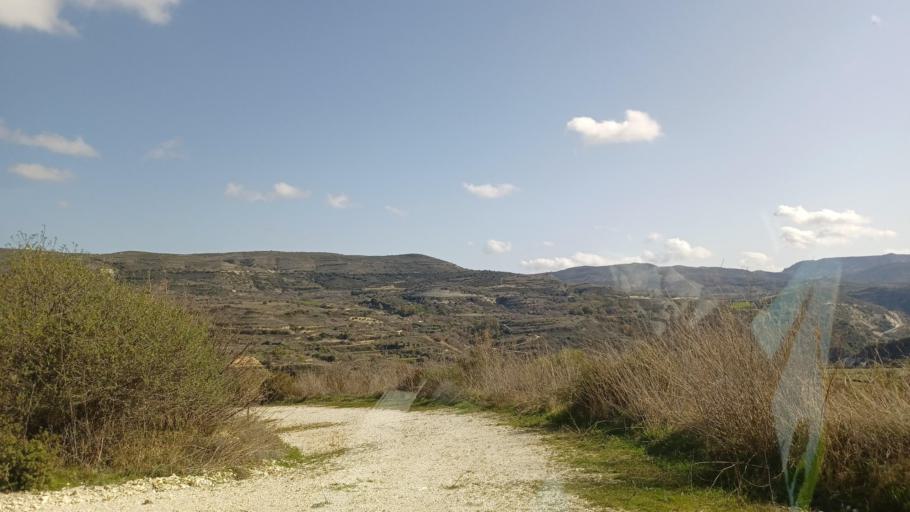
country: CY
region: Limassol
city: Pachna
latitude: 34.8390
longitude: 32.7175
